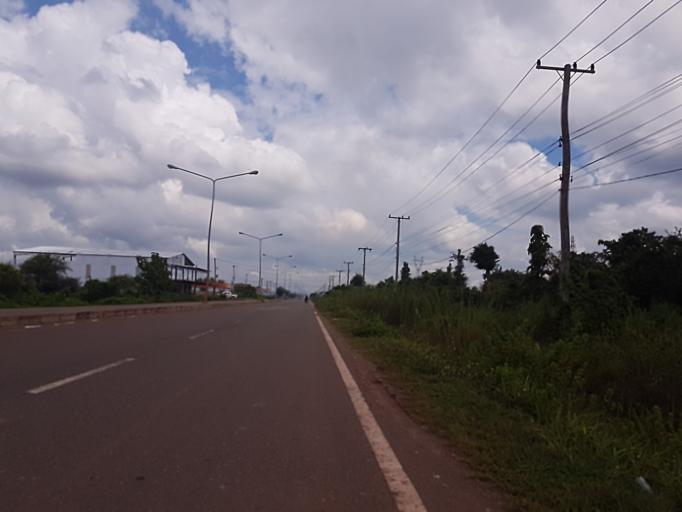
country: LA
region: Vientiane
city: Vientiane
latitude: 18.0070
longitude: 102.7208
